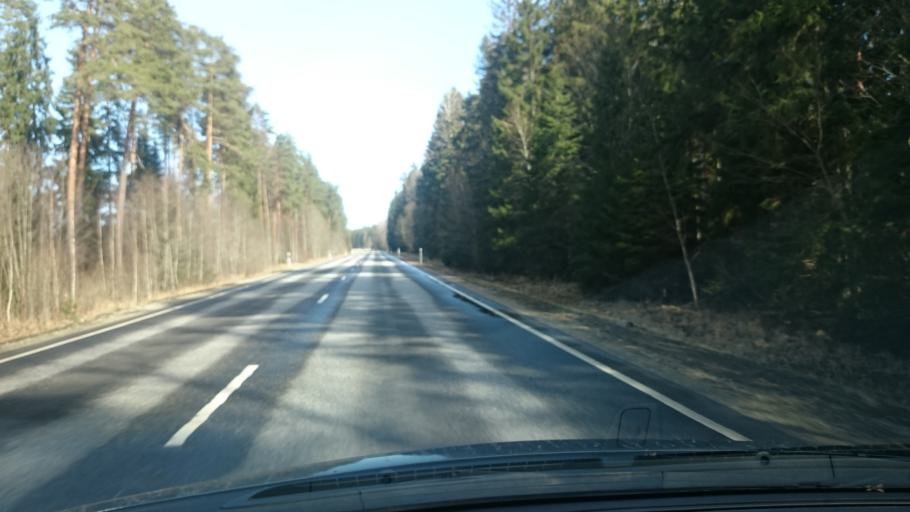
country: EE
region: Paernumaa
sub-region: Vaendra vald (alev)
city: Vandra
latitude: 58.6814
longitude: 25.2327
